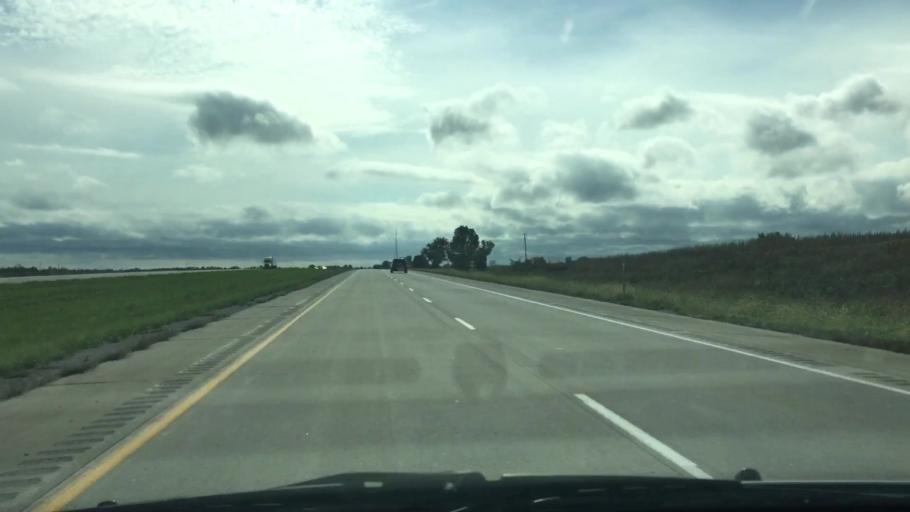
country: US
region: Iowa
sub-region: Decatur County
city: Leon
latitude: 40.8325
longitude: -93.8129
